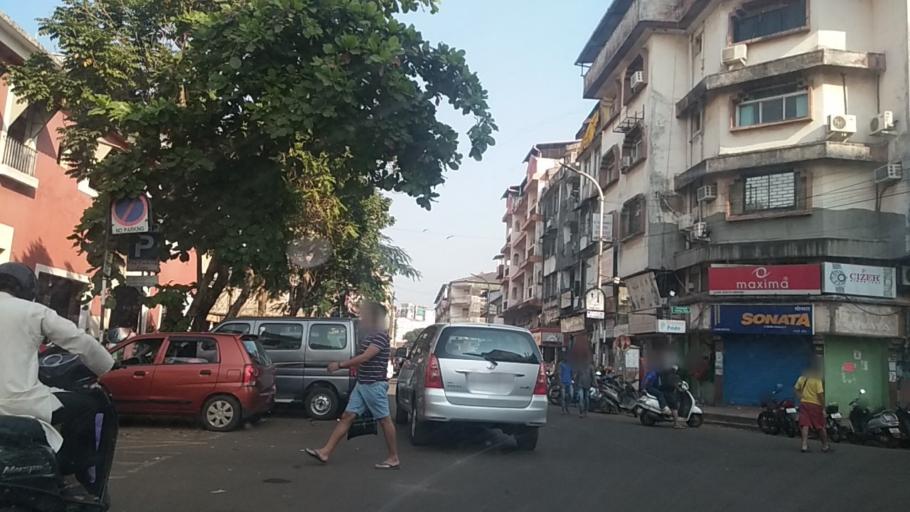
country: IN
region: Goa
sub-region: North Goa
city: Panaji
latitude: 15.4985
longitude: 73.8221
